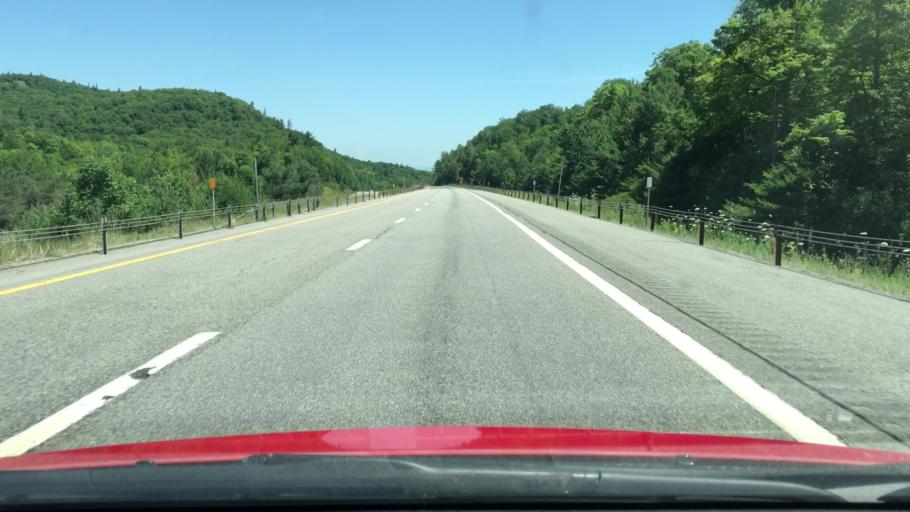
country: US
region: New York
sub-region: Essex County
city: Elizabethtown
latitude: 44.1823
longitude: -73.5716
